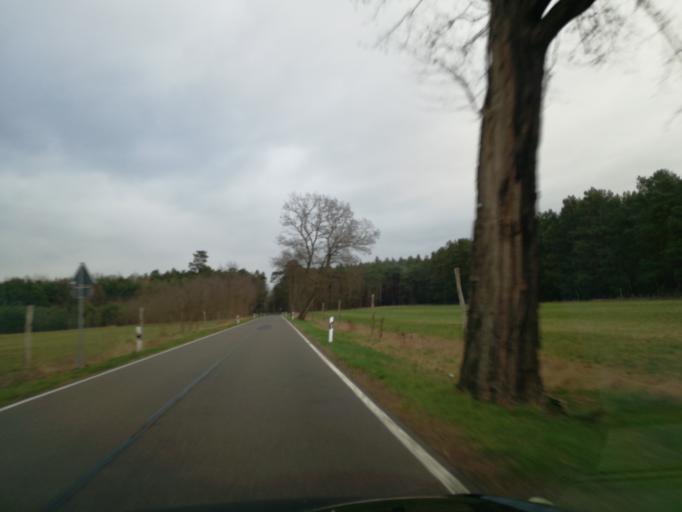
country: DE
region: Brandenburg
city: Vetschau
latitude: 51.7384
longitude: 14.1301
